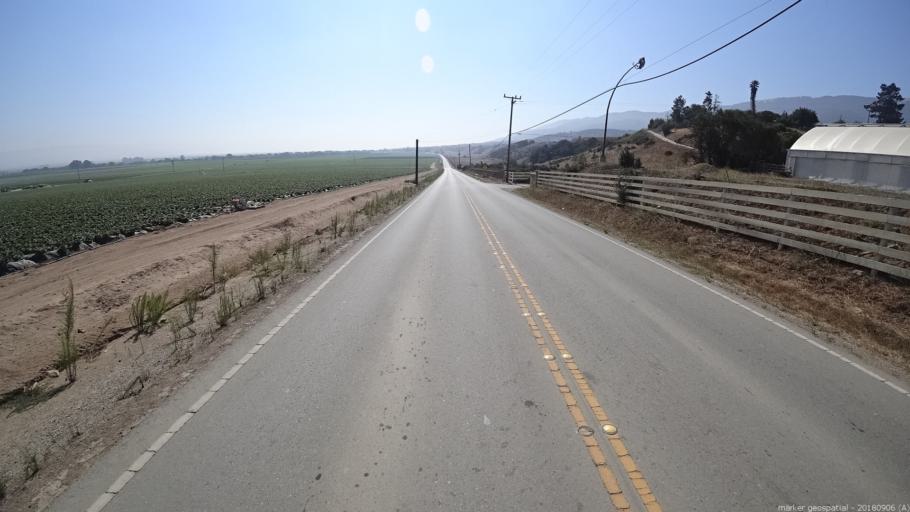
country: US
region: California
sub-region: Monterey County
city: Chualar
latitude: 36.5869
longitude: -121.6019
